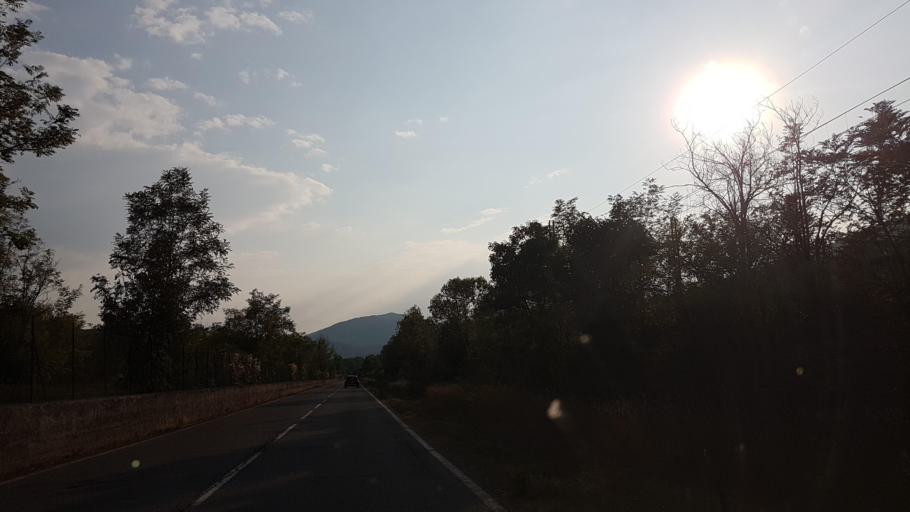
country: IT
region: Emilia-Romagna
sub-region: Provincia di Parma
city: Solignano
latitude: 44.6017
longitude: 9.9690
